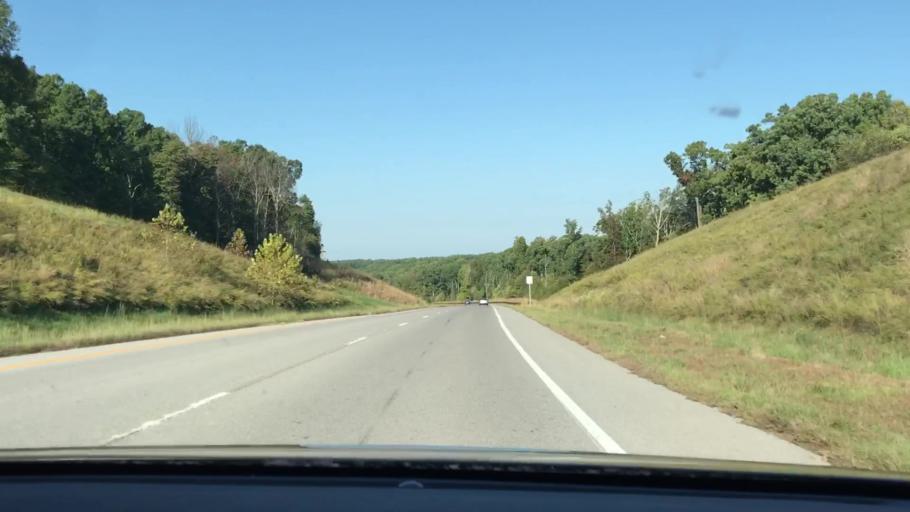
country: US
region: Kentucky
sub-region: Trigg County
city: Cadiz
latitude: 36.7789
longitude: -88.0820
